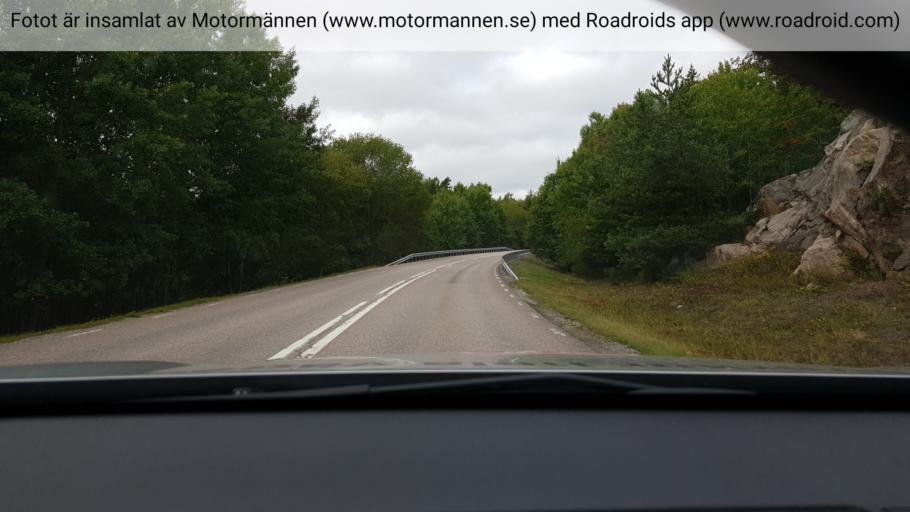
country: SE
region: Stockholm
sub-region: Vaxholms Kommun
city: Vaxholm
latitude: 59.3936
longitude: 18.4092
